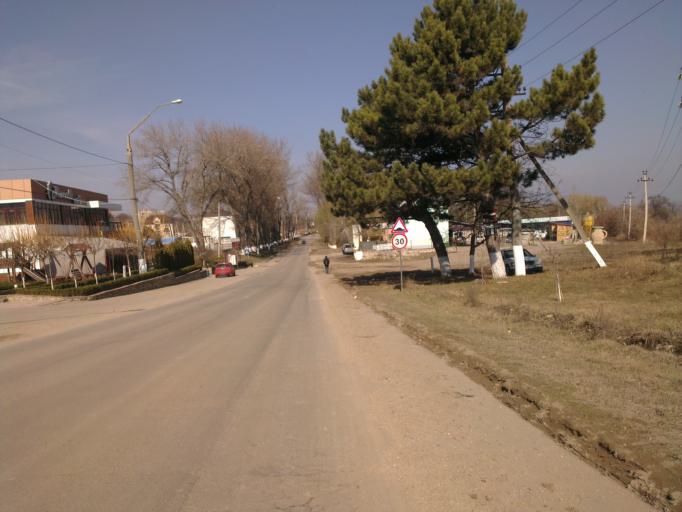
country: MD
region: Chisinau
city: Cricova
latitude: 47.1245
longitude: 28.8656
